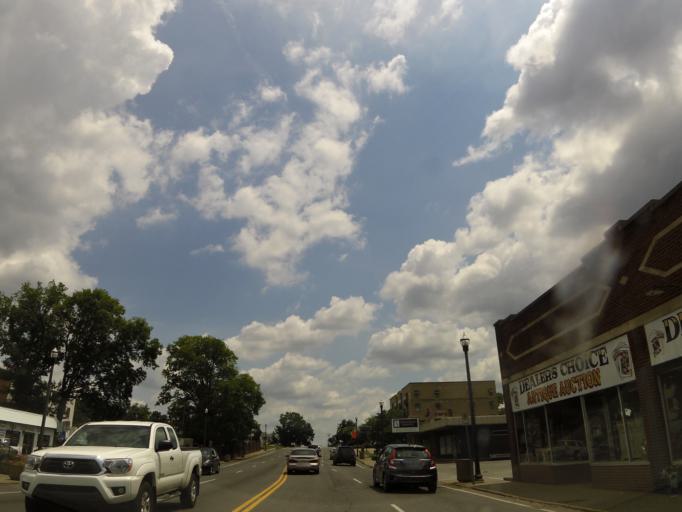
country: US
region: Tennessee
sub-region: Davidson County
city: Nashville
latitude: 36.1316
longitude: -86.7789
